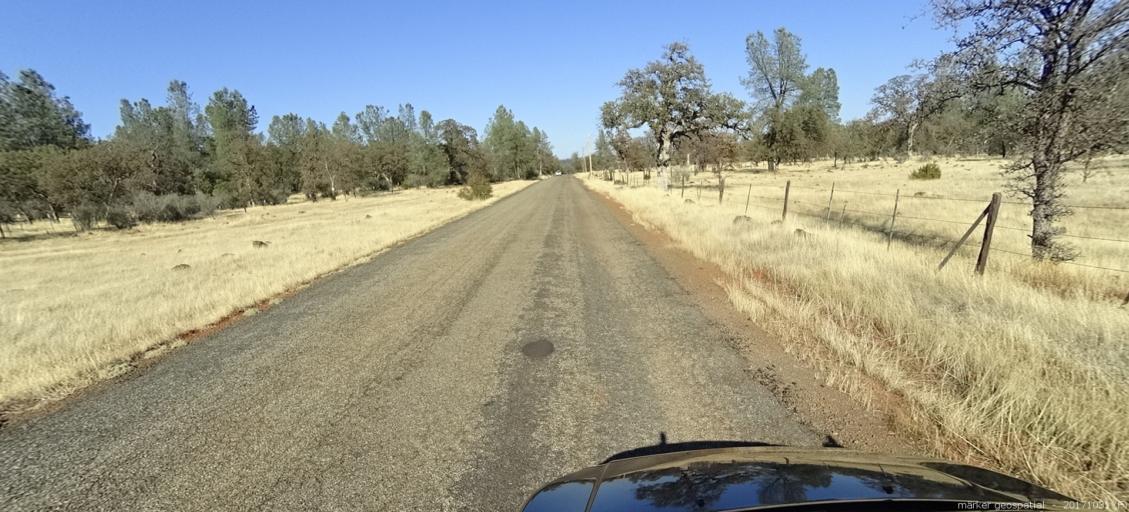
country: US
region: California
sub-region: Shasta County
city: Palo Cedro
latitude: 40.4765
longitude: -122.0866
